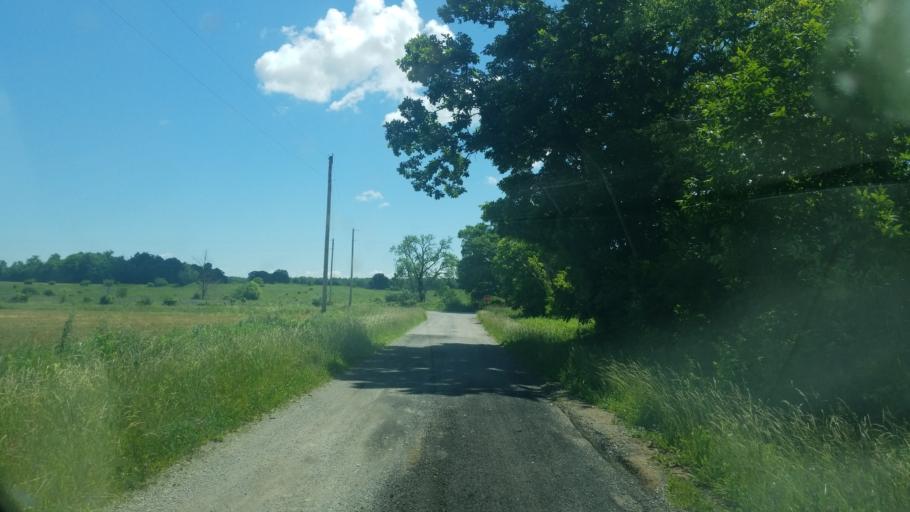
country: US
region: Ohio
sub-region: Huron County
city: New London
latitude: 41.1506
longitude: -82.3907
